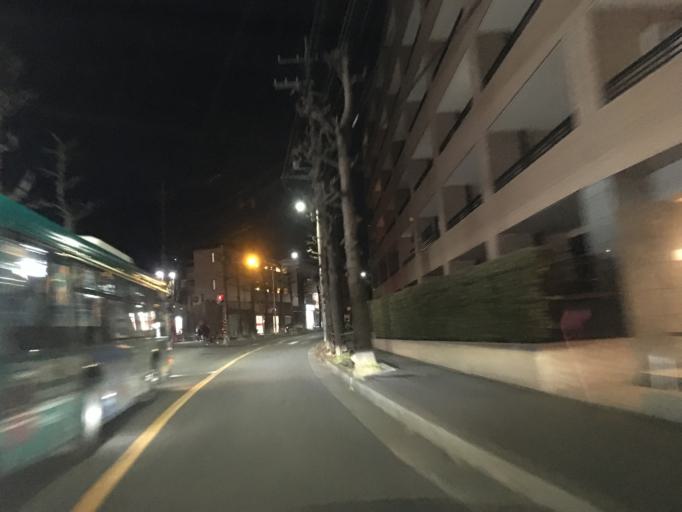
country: JP
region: Tokyo
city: Chofugaoka
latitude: 35.6150
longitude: 139.5224
